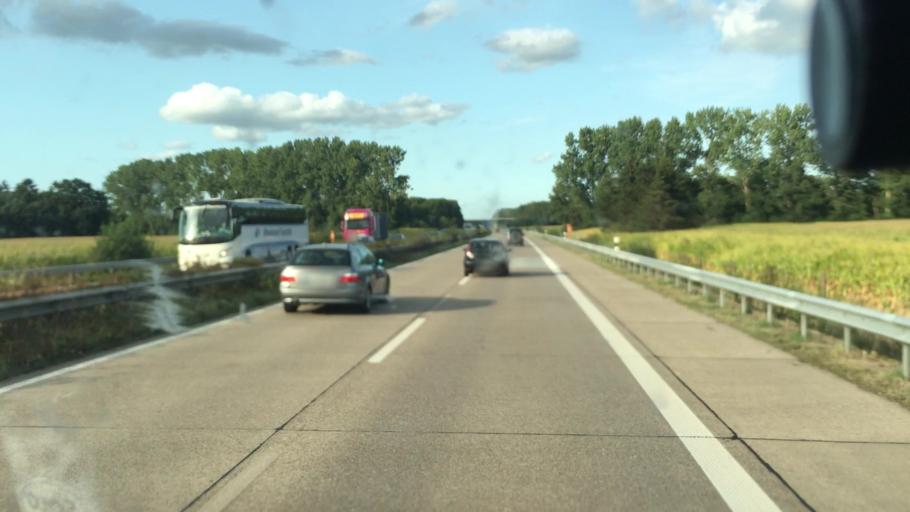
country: DE
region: Lower Saxony
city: Wardenburg
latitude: 53.0893
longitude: 8.2604
